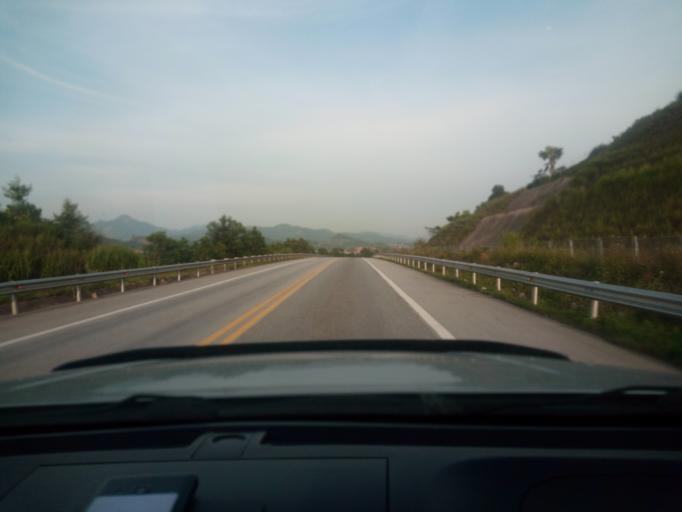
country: VN
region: Yen Bai
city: Co Phuc
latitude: 21.8863
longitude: 104.6619
